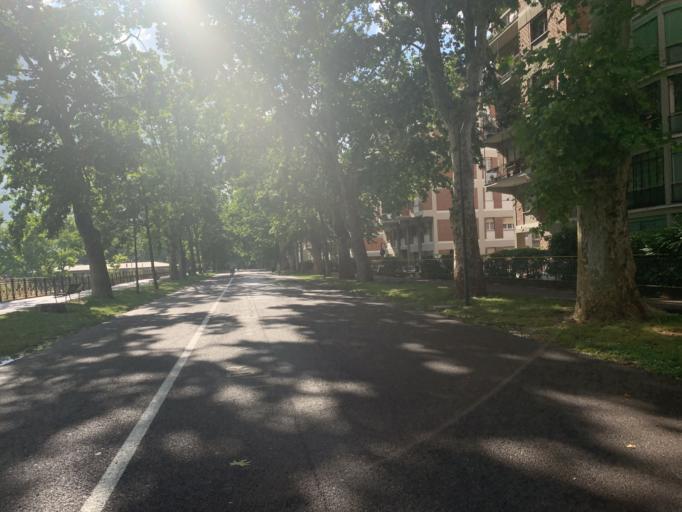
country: IT
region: Emilia-Romagna
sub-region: Provincia di Piacenza
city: Piacenza
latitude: 45.0454
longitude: 9.6945
